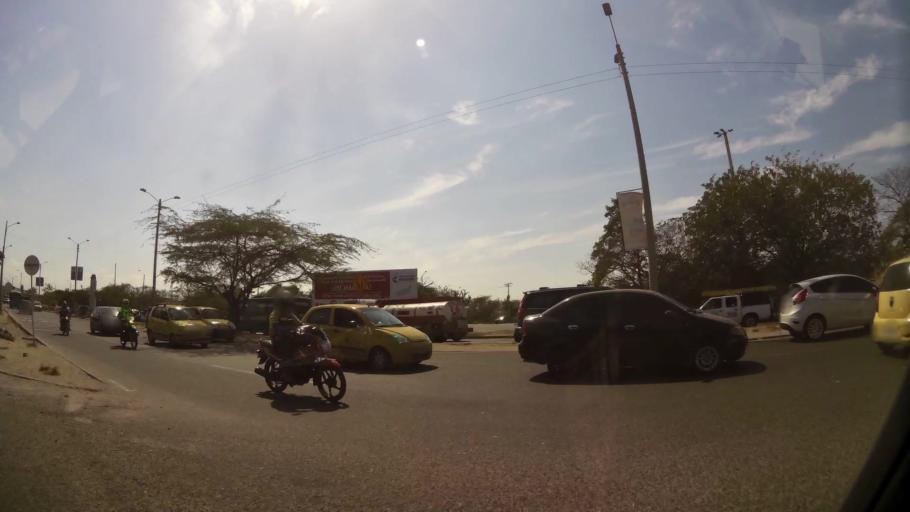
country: CO
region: Atlantico
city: Barranquilla
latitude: 10.9429
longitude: -74.8337
